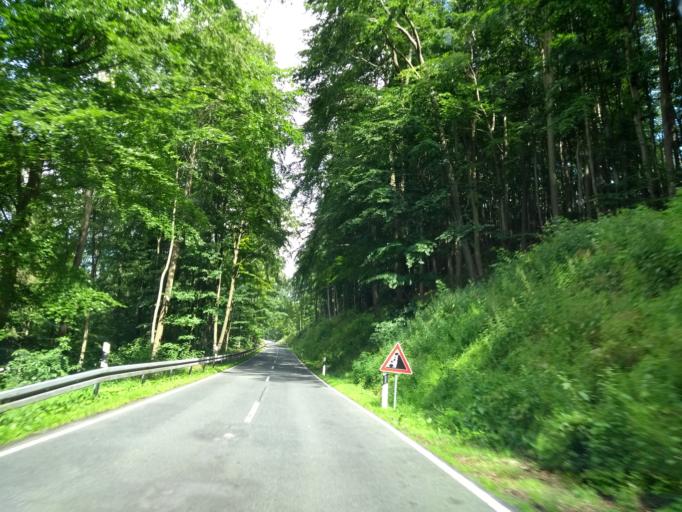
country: DE
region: Lower Saxony
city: Bad Pyrmont
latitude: 51.9654
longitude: 9.2982
